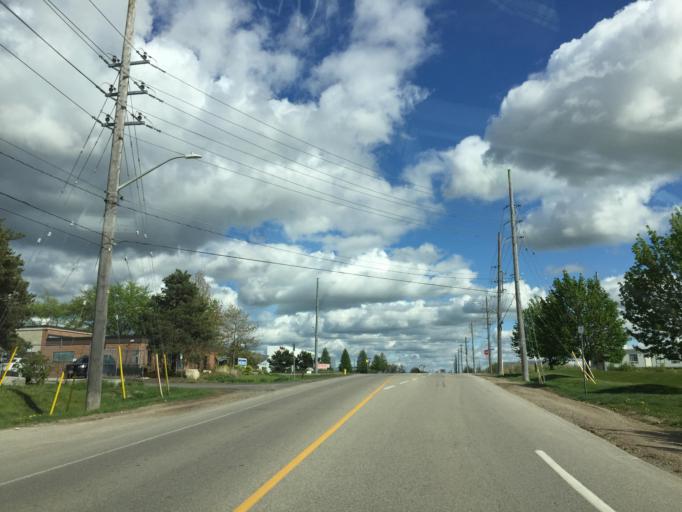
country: CA
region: Ontario
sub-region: Wellington County
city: Guelph
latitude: 43.4901
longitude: -80.2044
